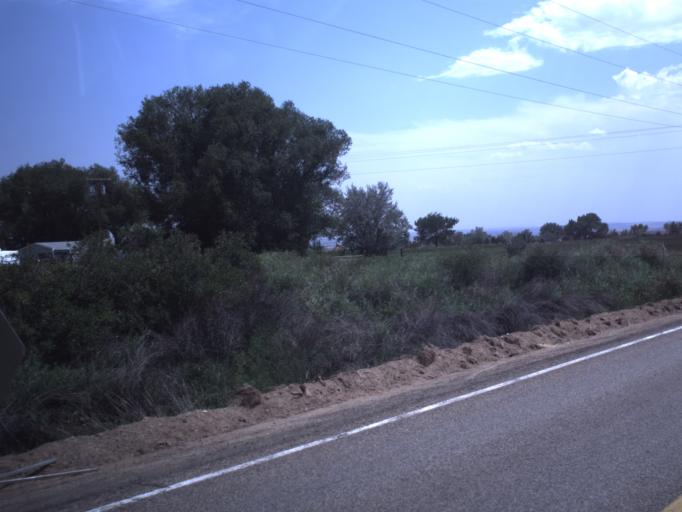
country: US
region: Utah
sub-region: Duchesne County
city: Roosevelt
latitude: 40.3859
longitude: -110.0298
